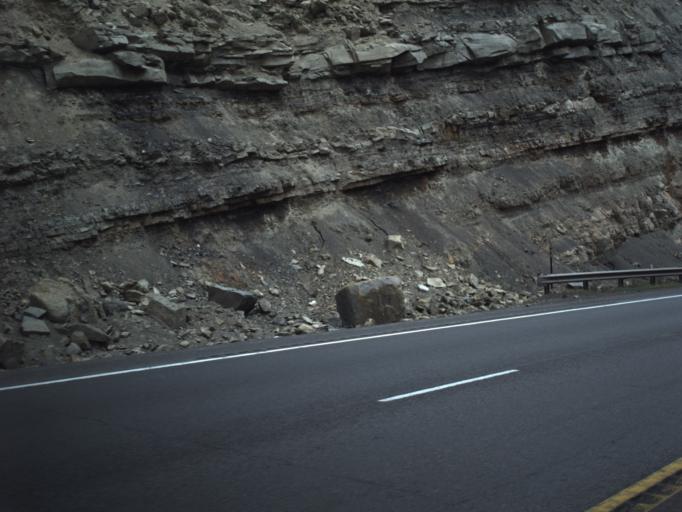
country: US
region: Utah
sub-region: Carbon County
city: Helper
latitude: 39.7989
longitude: -110.9320
